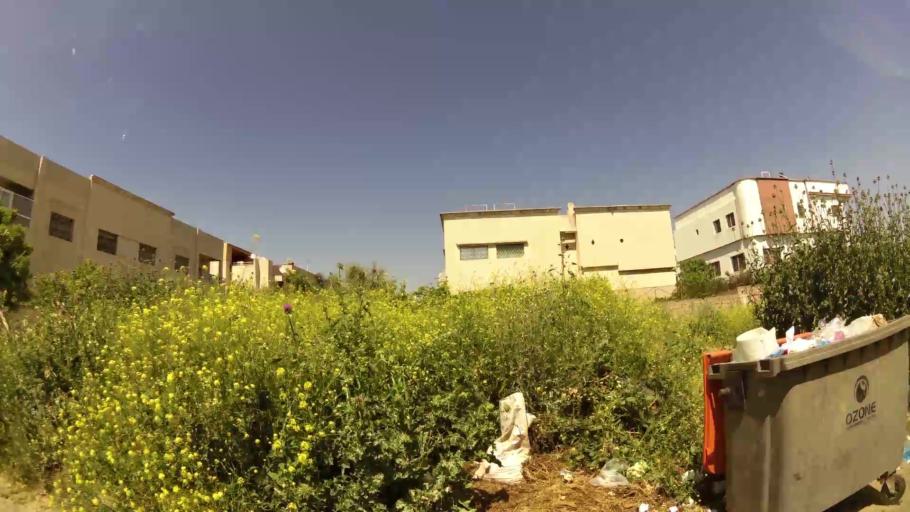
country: MA
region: Fes-Boulemane
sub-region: Fes
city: Fes
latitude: 34.0177
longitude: -5.0239
